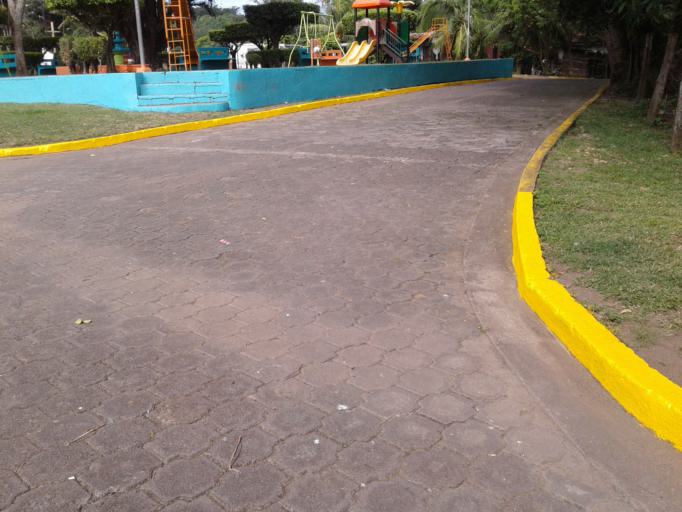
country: NI
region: Rivas
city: Cardenas
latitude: 11.2464
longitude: -85.6247
